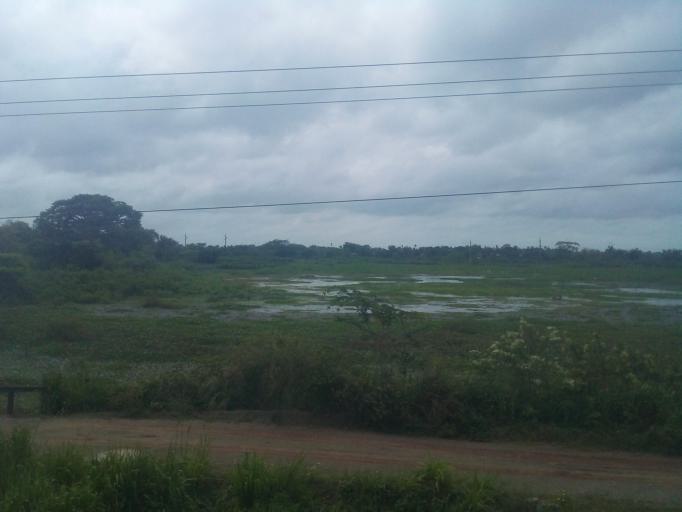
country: BR
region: Maranhao
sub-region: Arari
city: Arari
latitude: -3.5685
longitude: -44.6838
